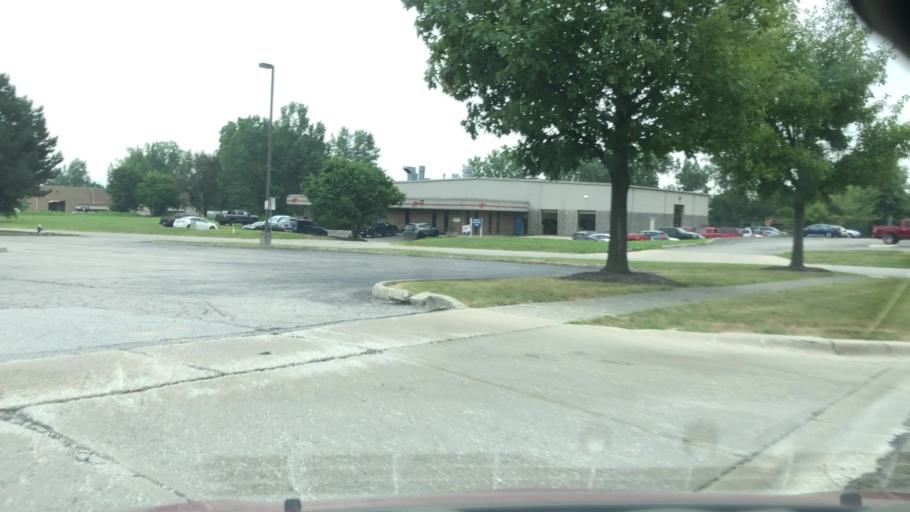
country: US
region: Ohio
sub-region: Franklin County
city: Hilliard
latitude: 40.0318
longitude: -83.1290
